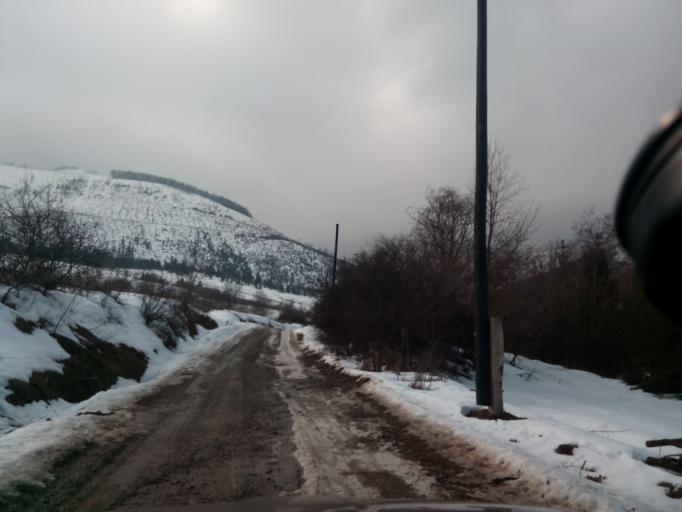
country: SK
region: Presovsky
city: Stara L'ubovna
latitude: 49.2188
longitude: 20.7503
